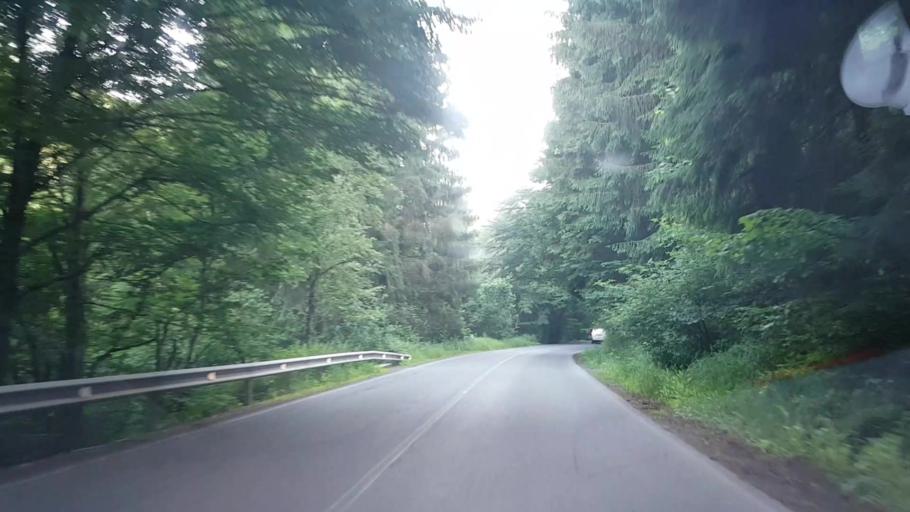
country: RO
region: Harghita
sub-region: Comuna Praid
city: Ocna de Sus
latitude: 46.5836
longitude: 25.2429
